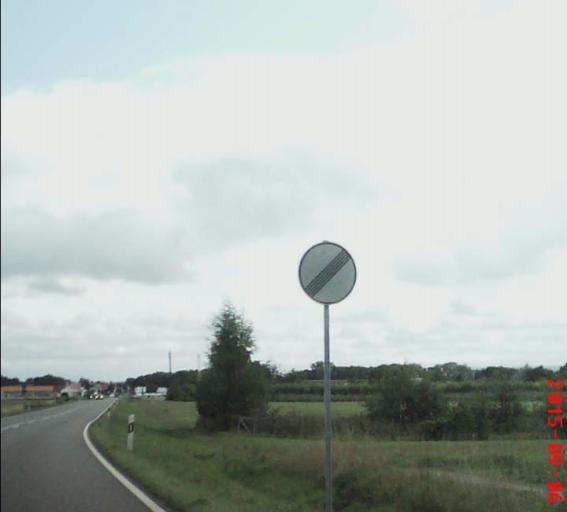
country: DE
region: Thuringia
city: Muehlhausen
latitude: 51.2477
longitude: 10.4518
